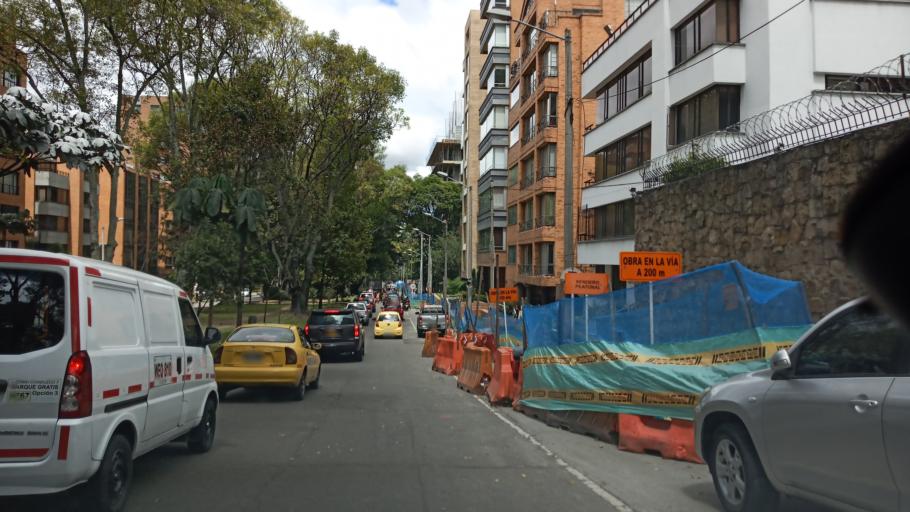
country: CO
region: Bogota D.C.
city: Barrio San Luis
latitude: 4.6719
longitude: -74.0445
